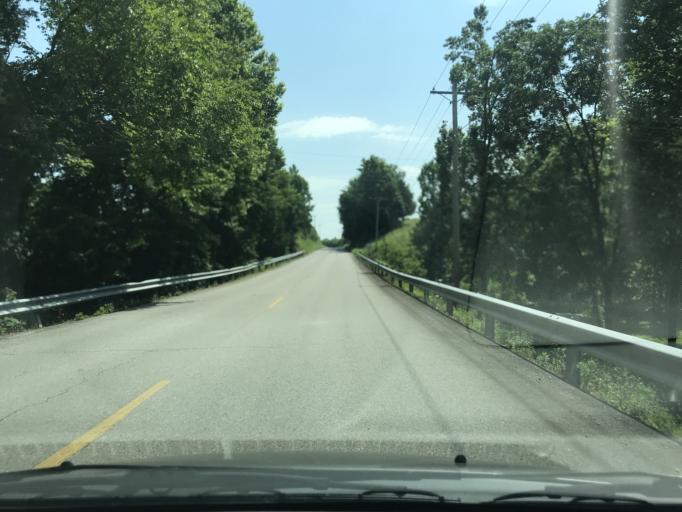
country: US
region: Tennessee
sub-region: Loudon County
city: Lenoir City
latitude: 35.8201
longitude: -84.3319
